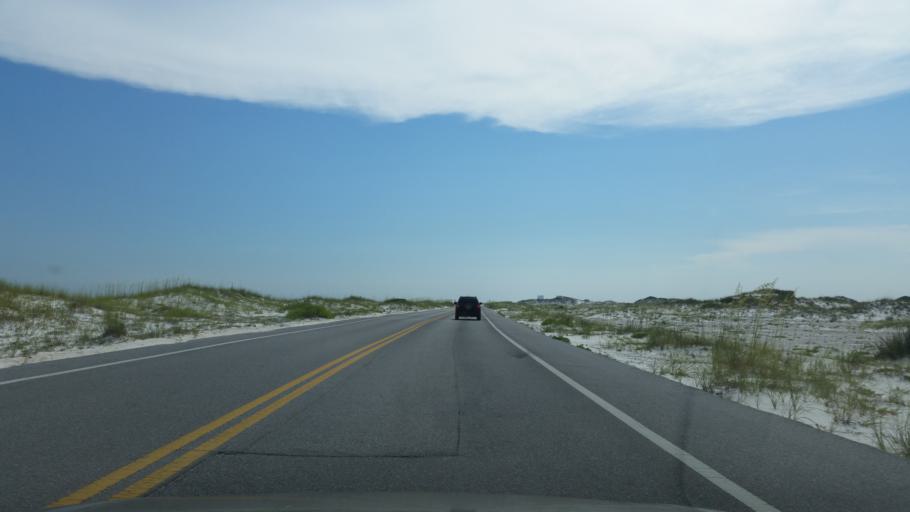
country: US
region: Florida
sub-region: Santa Rosa County
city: Woodlawn Beach
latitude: 30.3555
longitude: -87.0147
